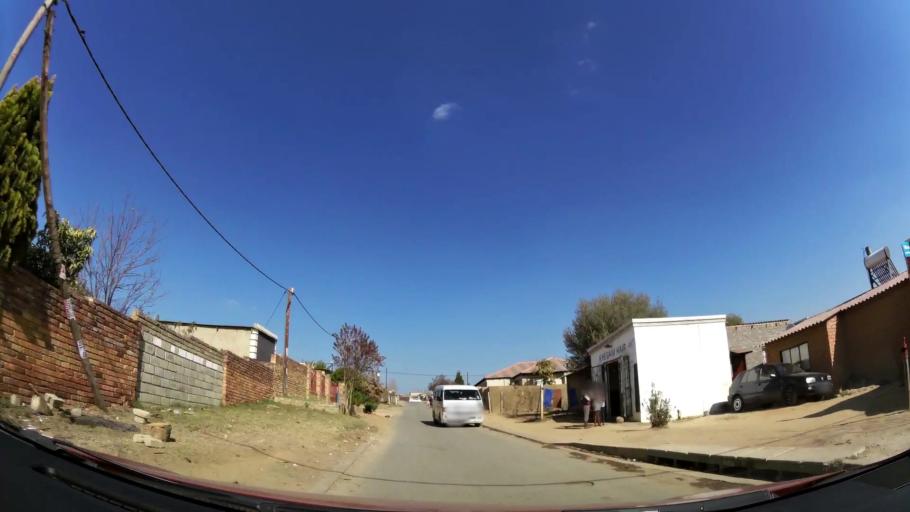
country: ZA
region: Gauteng
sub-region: West Rand District Municipality
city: Muldersdriseloop
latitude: -26.0168
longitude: 27.9243
